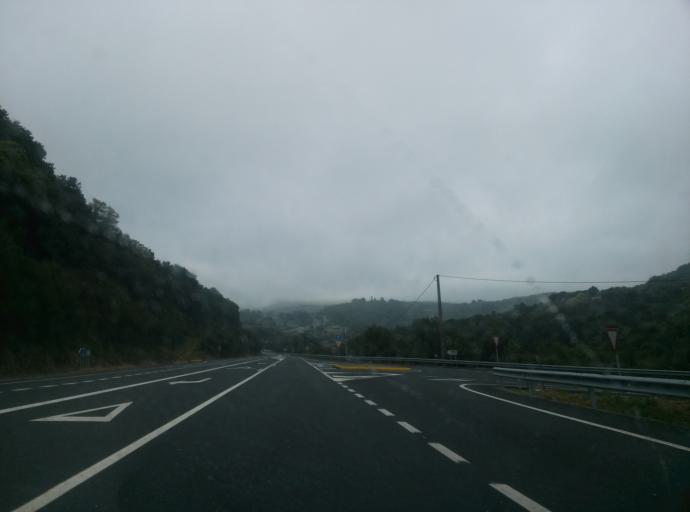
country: ES
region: Galicia
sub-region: Provincia de Lugo
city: Muras
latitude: 43.4478
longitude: -7.7272
